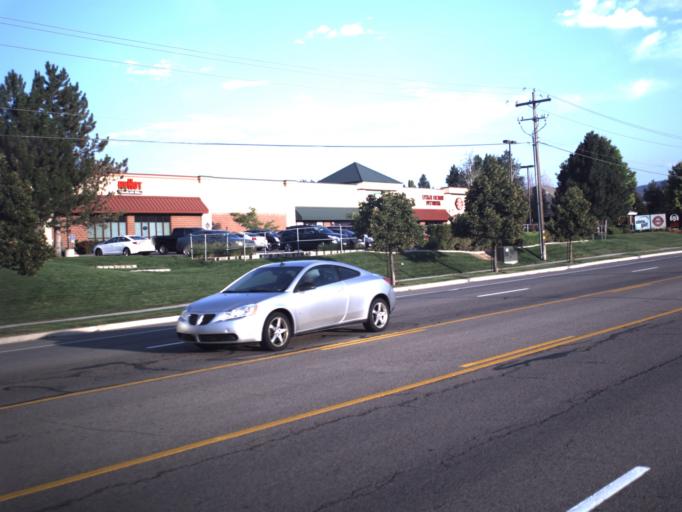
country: US
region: Utah
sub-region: Salt Lake County
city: White City
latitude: 40.5551
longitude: -111.8909
